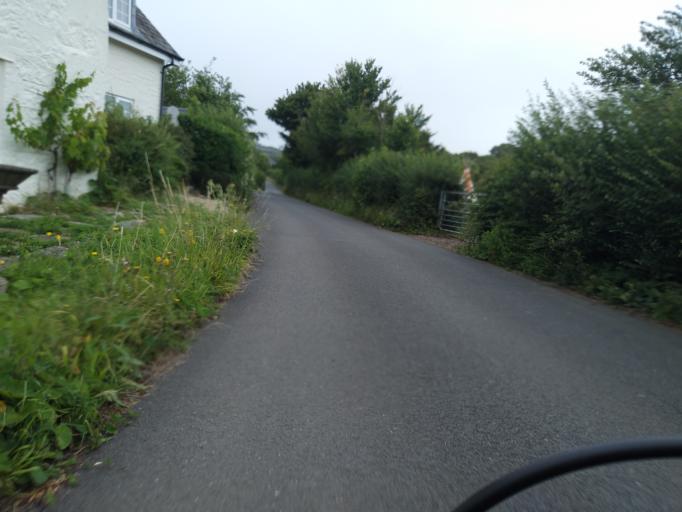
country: GB
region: England
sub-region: Isle of Wight
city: Sandown
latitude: 50.6686
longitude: -1.1640
